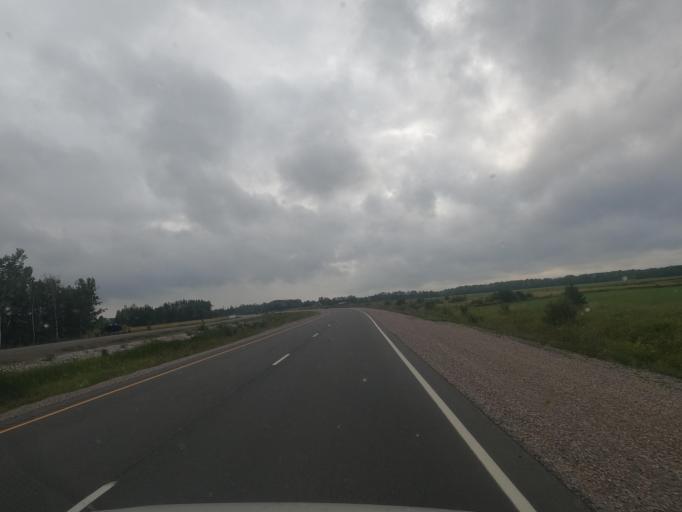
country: CA
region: Ontario
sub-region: Algoma
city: Sault Ste. Marie
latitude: 46.4499
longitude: -84.0649
